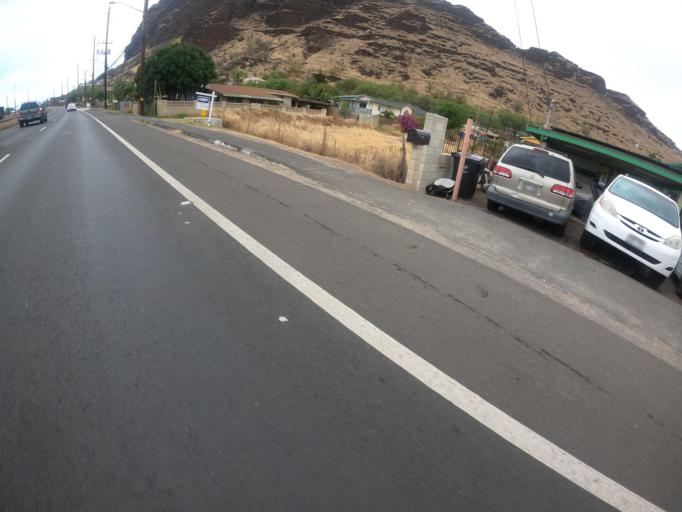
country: US
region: Hawaii
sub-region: Honolulu County
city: Nanakuli
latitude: 21.3974
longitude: -158.1649
